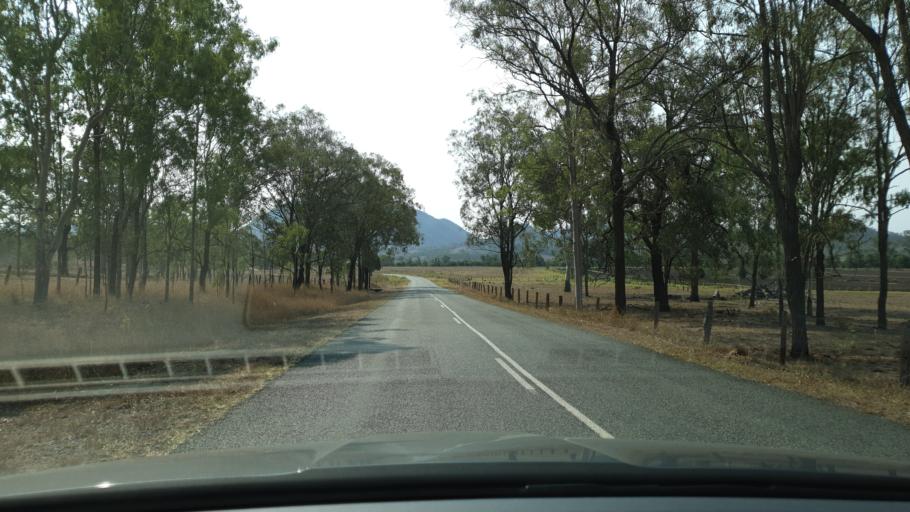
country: AU
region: Queensland
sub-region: Logan
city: Cedar Vale
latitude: -28.1399
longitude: 152.6036
